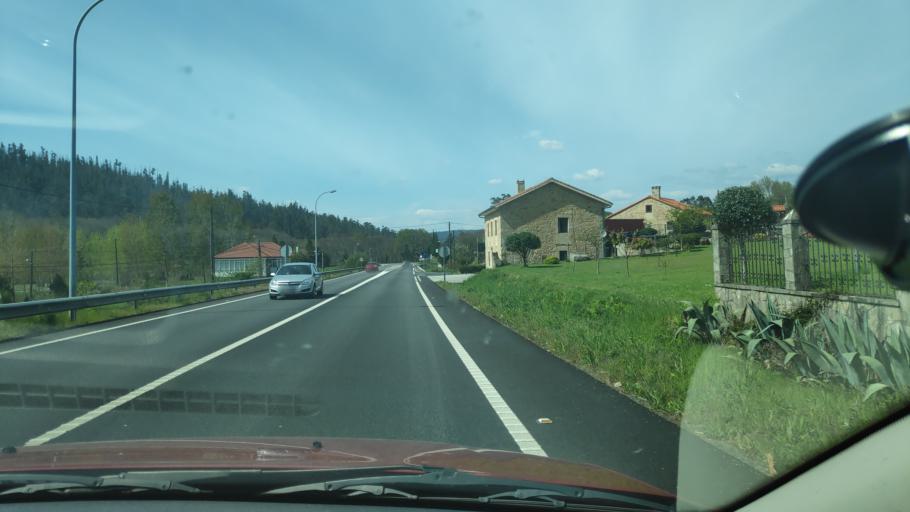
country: ES
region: Galicia
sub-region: Provincia da Coruna
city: Ames
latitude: 42.8835
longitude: -8.6820
